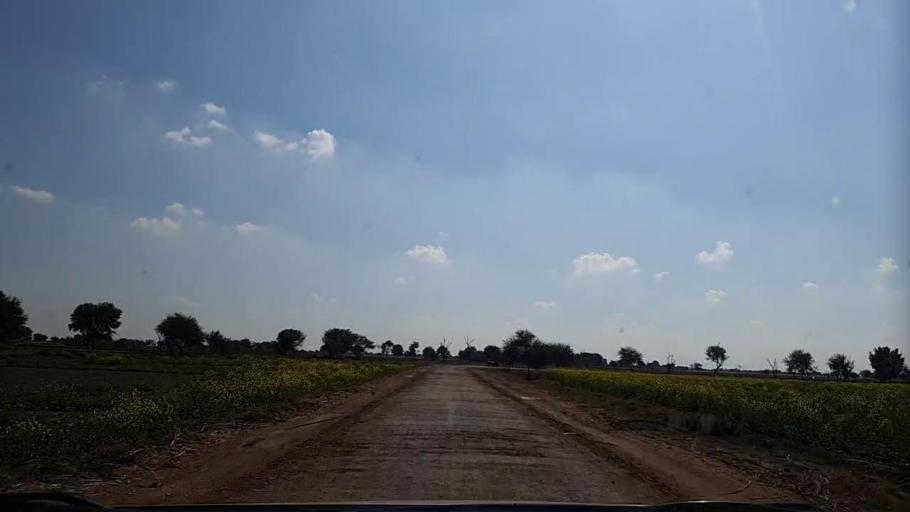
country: PK
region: Sindh
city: Pithoro
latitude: 25.6674
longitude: 69.4618
